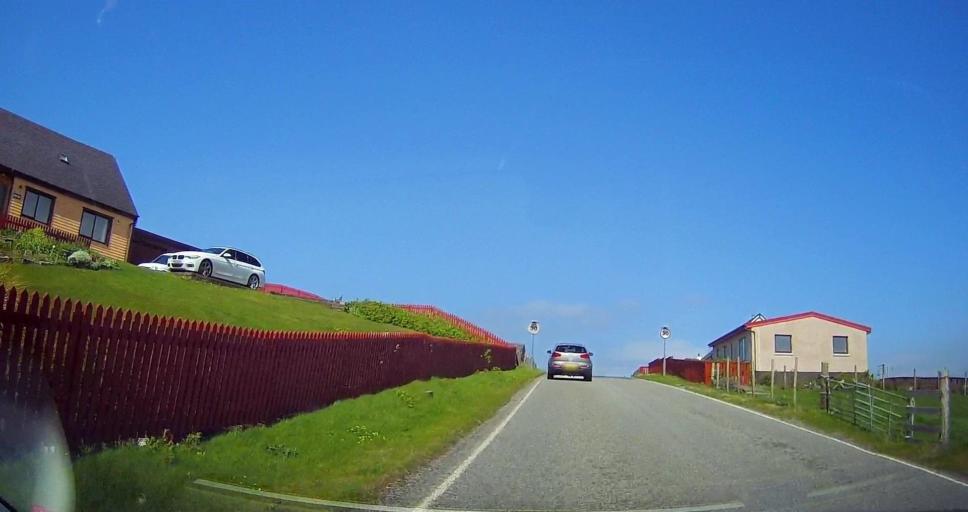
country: GB
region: Scotland
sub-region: Shetland Islands
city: Sandwick
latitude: 60.0954
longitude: -1.3217
